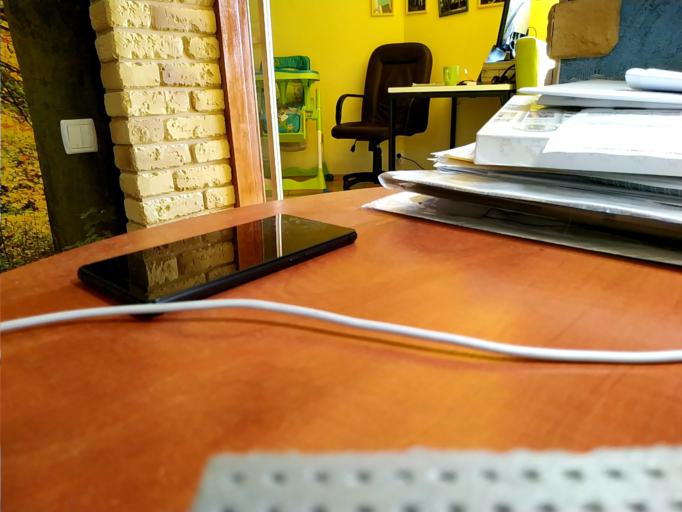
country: RU
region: Tverskaya
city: Kalashnikovo
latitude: 57.3876
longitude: 35.3092
